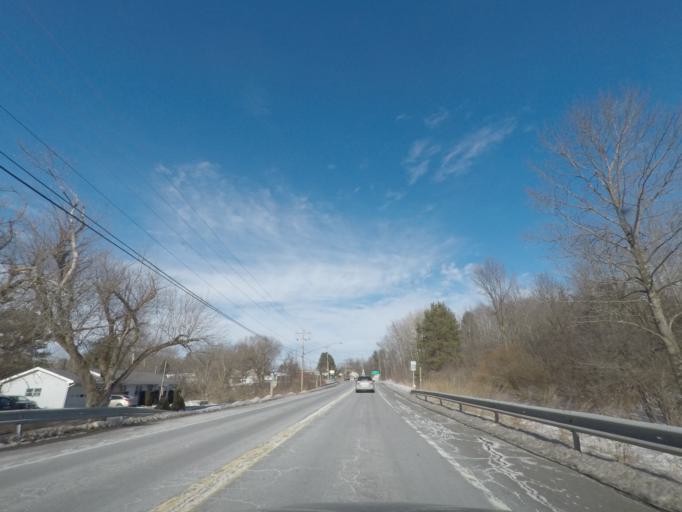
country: US
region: New York
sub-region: Schenectady County
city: Rotterdam
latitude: 42.7334
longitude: -73.9864
